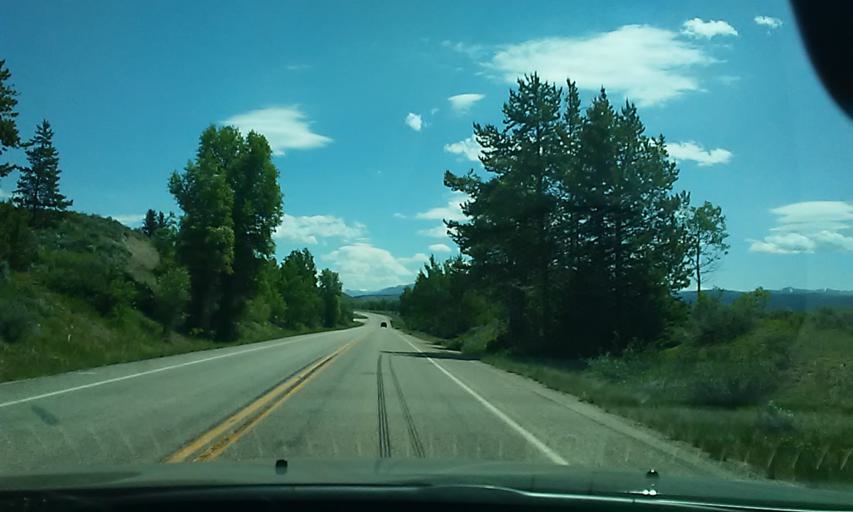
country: US
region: Wyoming
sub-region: Teton County
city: Jackson
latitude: 43.8391
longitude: -110.4738
